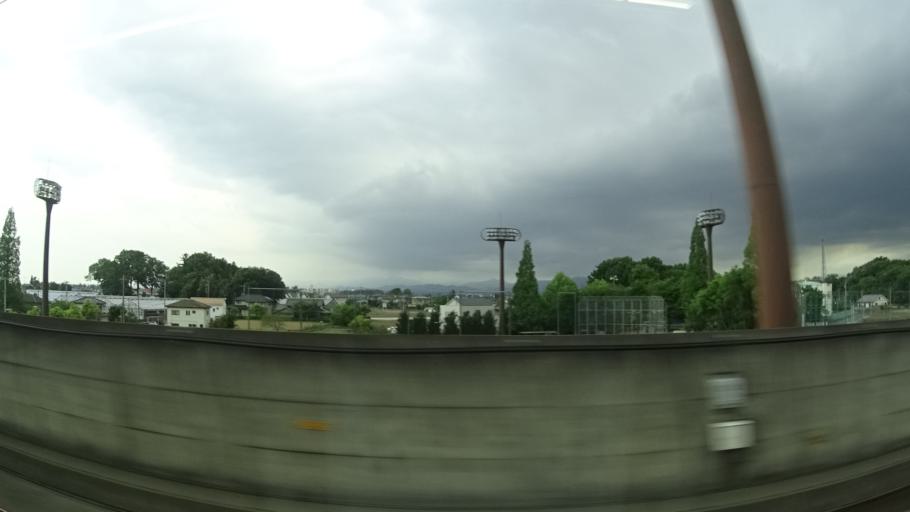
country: JP
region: Saitama
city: Fukayacho
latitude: 36.1755
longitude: 139.2684
